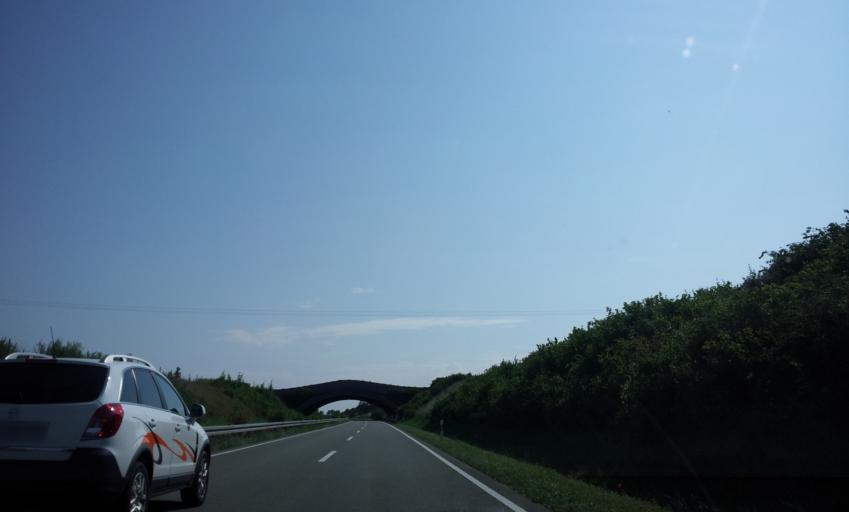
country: DE
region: Mecklenburg-Vorpommern
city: Brandshagen
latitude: 54.1536
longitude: 13.1699
